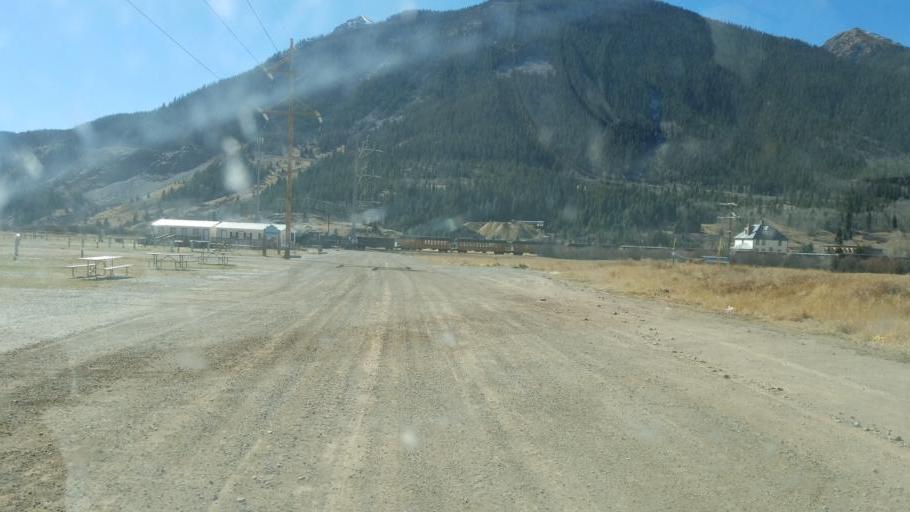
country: US
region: Colorado
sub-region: San Juan County
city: Silverton
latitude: 37.8059
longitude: -107.6669
